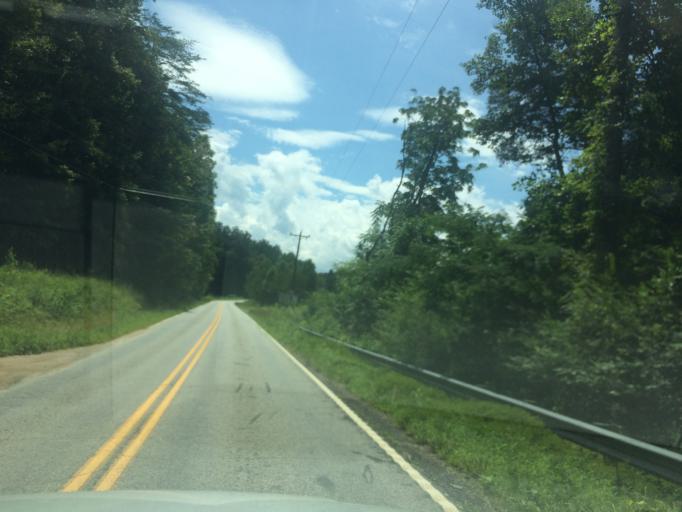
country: US
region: North Carolina
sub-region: Rutherford County
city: Lake Lure
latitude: 35.3807
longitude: -82.1910
